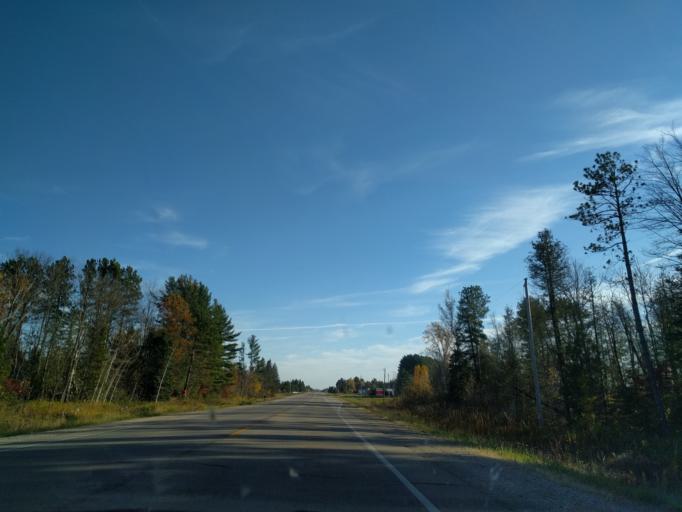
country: US
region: Wisconsin
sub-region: Marinette County
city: Niagara
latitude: 45.3925
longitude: -87.9629
